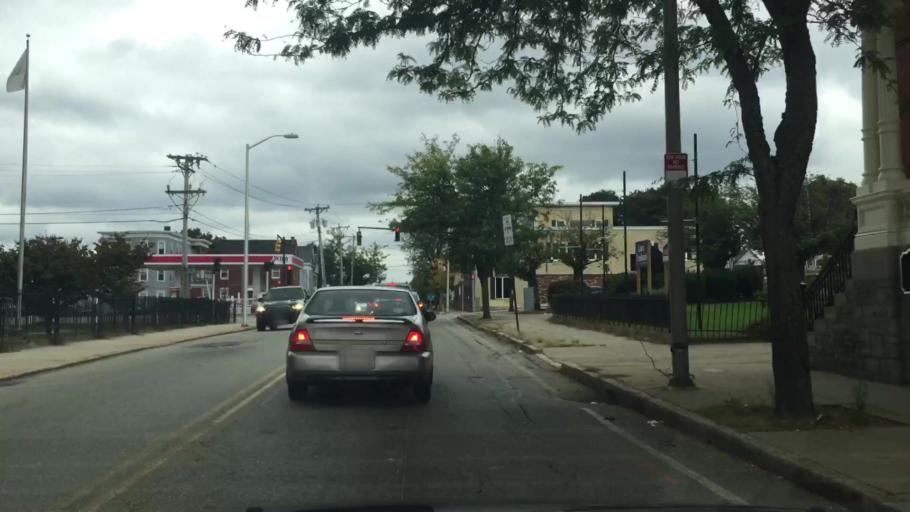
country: US
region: Massachusetts
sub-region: Middlesex County
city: Lowell
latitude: 42.6376
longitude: -71.3090
